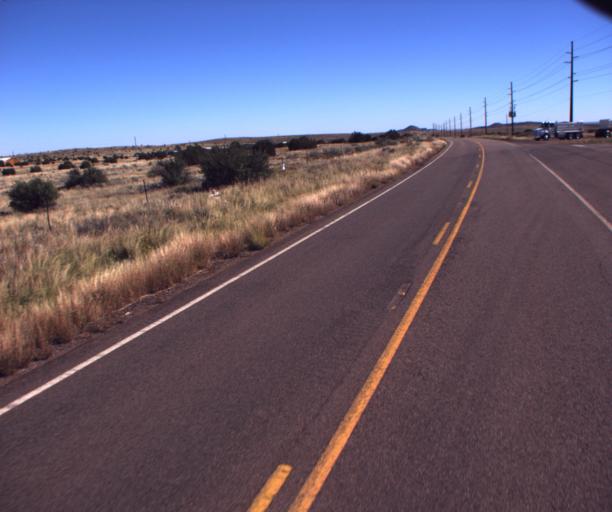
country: US
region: Arizona
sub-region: Navajo County
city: Taylor
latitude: 34.4854
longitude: -110.2454
